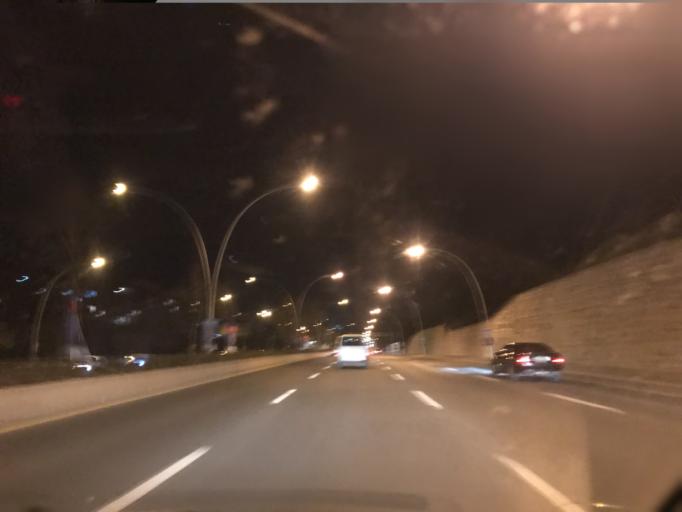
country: TR
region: Ankara
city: Ankara
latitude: 39.8725
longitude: 32.8109
